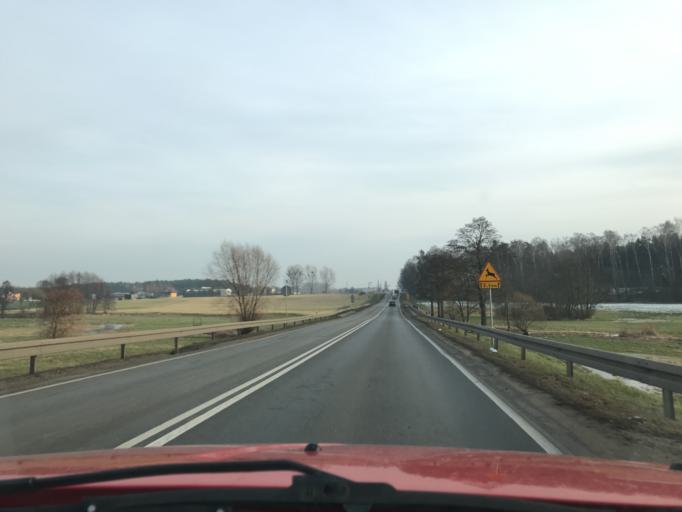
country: PL
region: Greater Poland Voivodeship
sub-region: Powiat jarocinski
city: Kotlin
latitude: 51.9369
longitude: 17.6075
